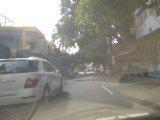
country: IN
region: Karnataka
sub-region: Bangalore Urban
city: Bangalore
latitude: 12.9856
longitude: 77.5383
